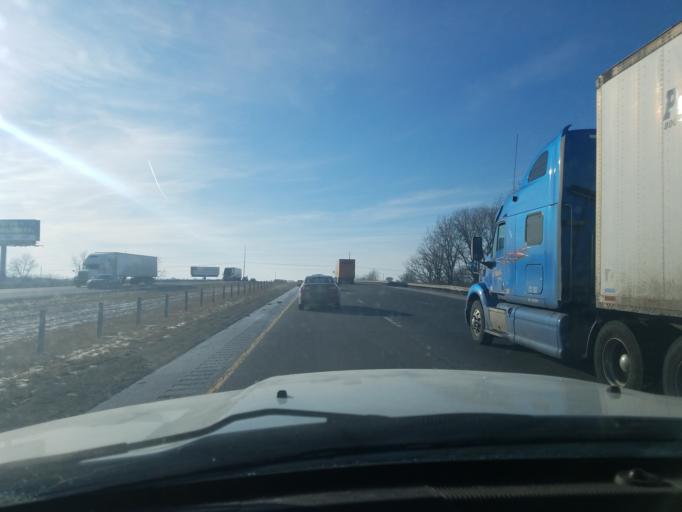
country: US
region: Indiana
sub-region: Madison County
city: Anderson
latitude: 40.0525
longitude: -85.6602
